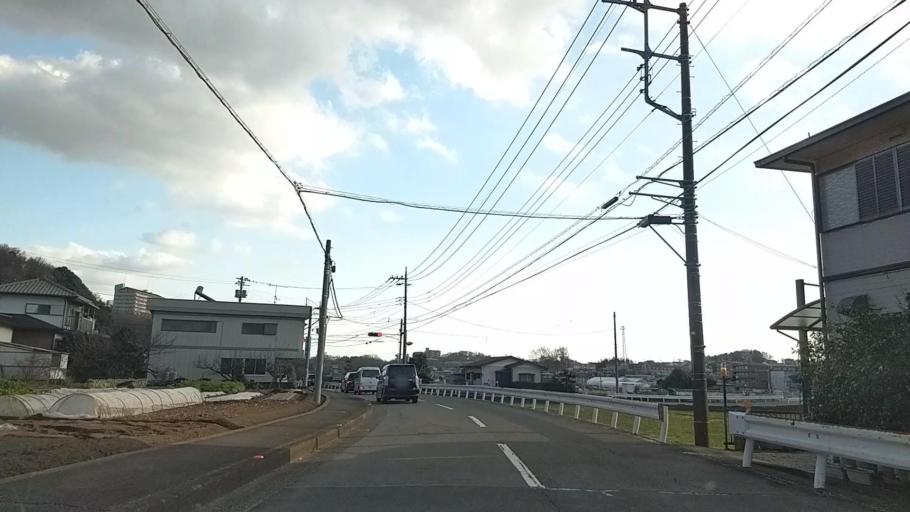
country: JP
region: Kanagawa
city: Atsugi
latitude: 35.4459
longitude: 139.3343
